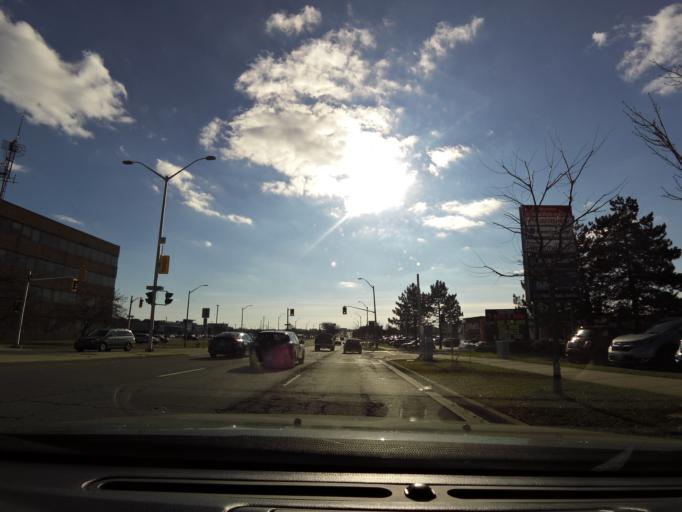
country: CA
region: Ontario
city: Hamilton
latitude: 43.2211
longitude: -79.8630
